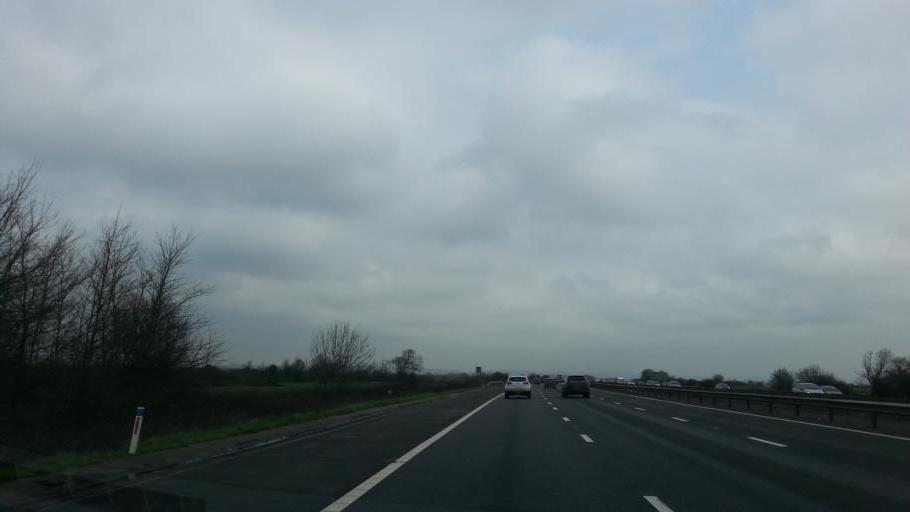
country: GB
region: England
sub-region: North Somerset
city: St. Georges
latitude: 51.3772
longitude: -2.8827
